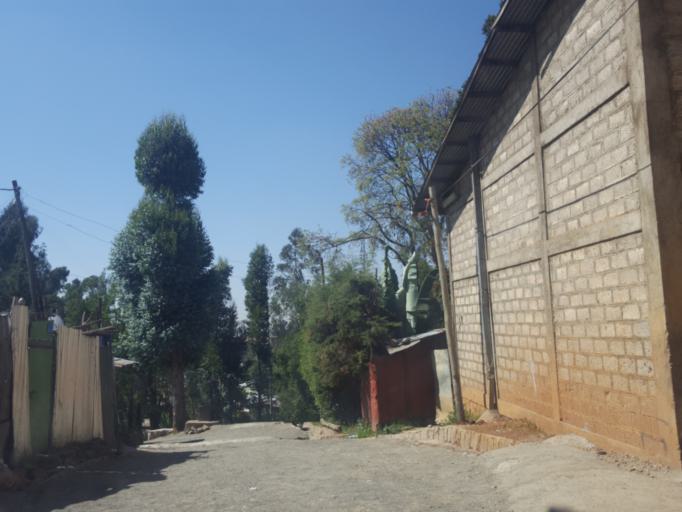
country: ET
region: Adis Abeba
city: Addis Ababa
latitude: 9.0565
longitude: 38.7400
